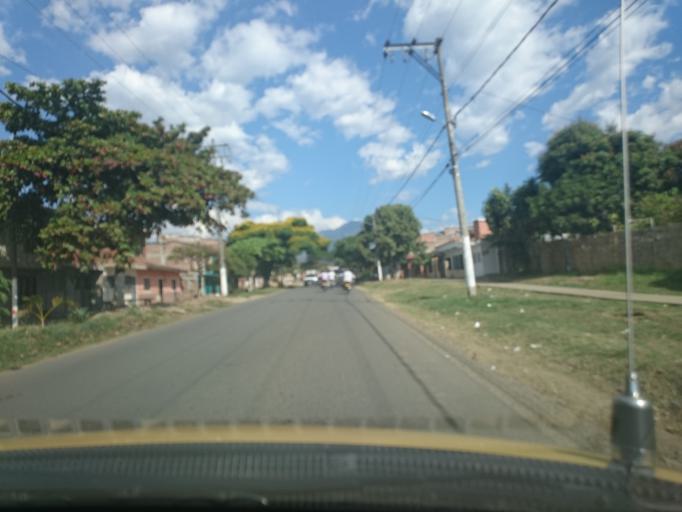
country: CO
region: Cauca
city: Santander de Quilichao
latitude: 3.0130
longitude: -76.4896
